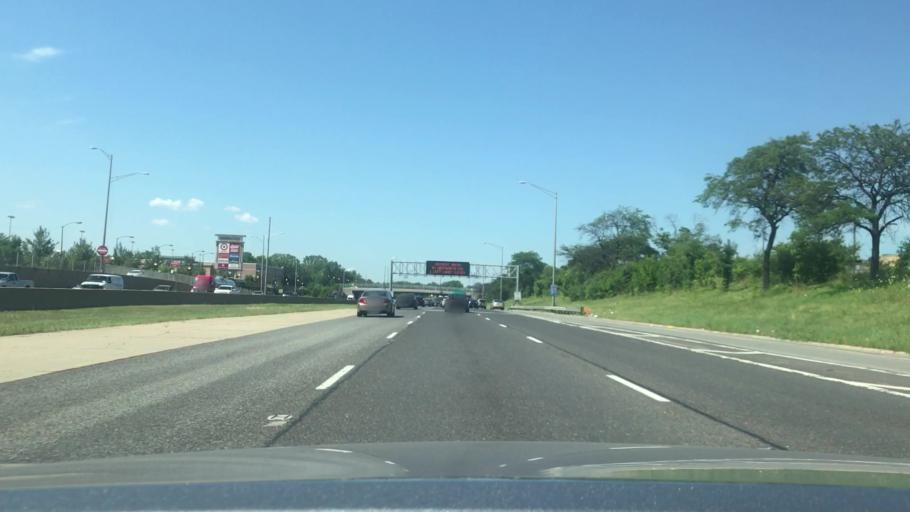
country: US
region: Illinois
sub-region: Cook County
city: Calumet Park
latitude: 41.6811
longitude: -87.6619
